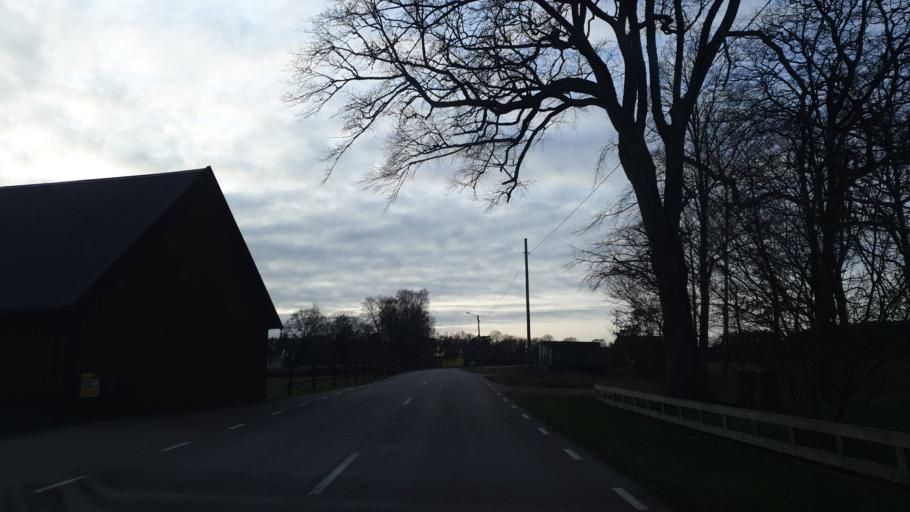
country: SE
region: Kalmar
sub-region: Torsas Kommun
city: Torsas
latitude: 56.2541
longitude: 16.0258
